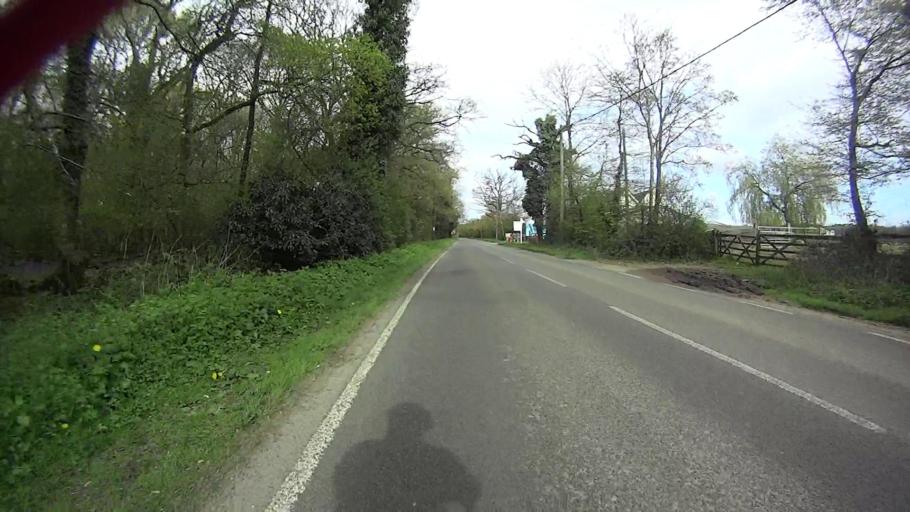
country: GB
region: England
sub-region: West Sussex
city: Langley Green
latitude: 51.1347
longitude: -0.2186
